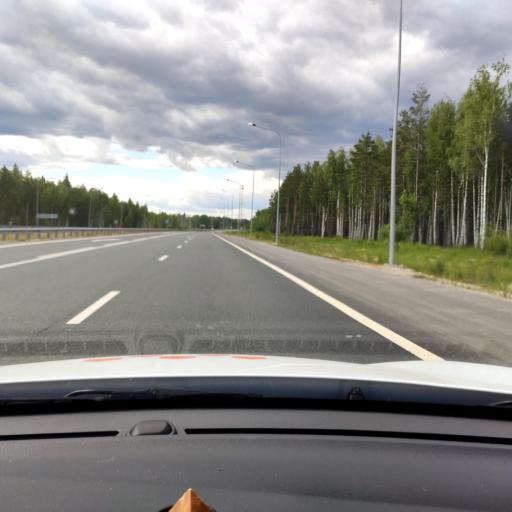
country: RU
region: Mariy-El
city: Surok
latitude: 56.4349
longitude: 48.1209
